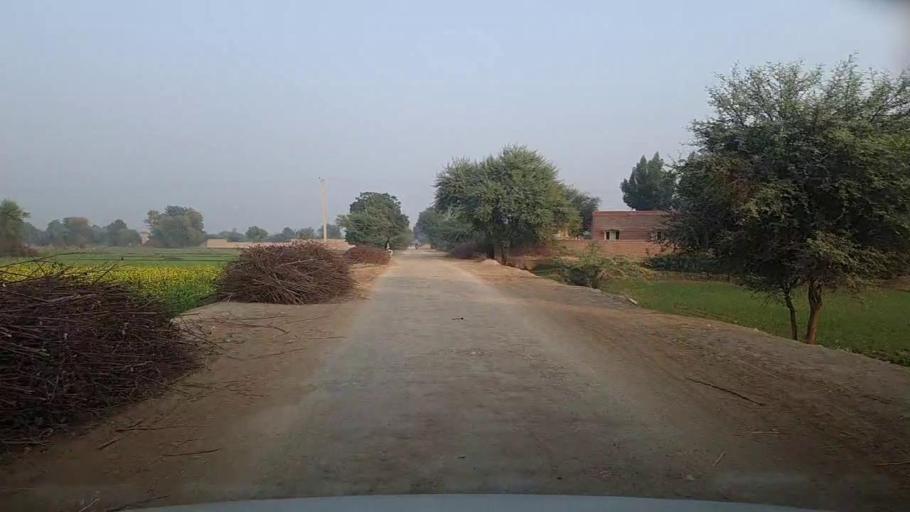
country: PK
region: Sindh
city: Bozdar
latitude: 27.0835
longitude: 68.5562
